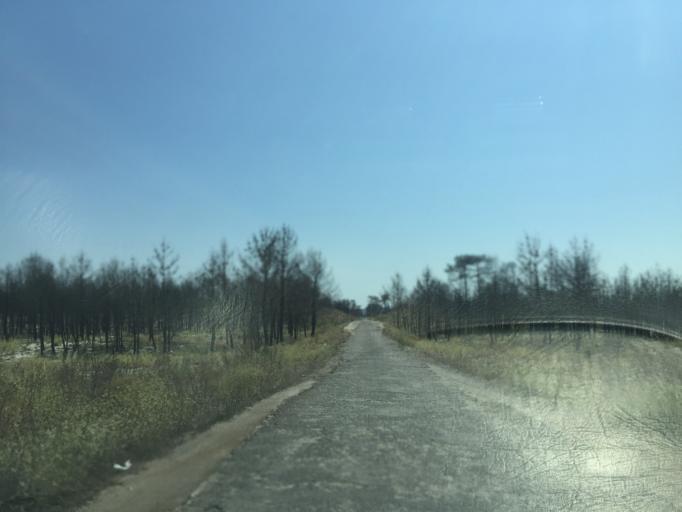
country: PT
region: Coimbra
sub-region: Figueira da Foz
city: Alhadas
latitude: 40.2892
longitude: -8.8230
